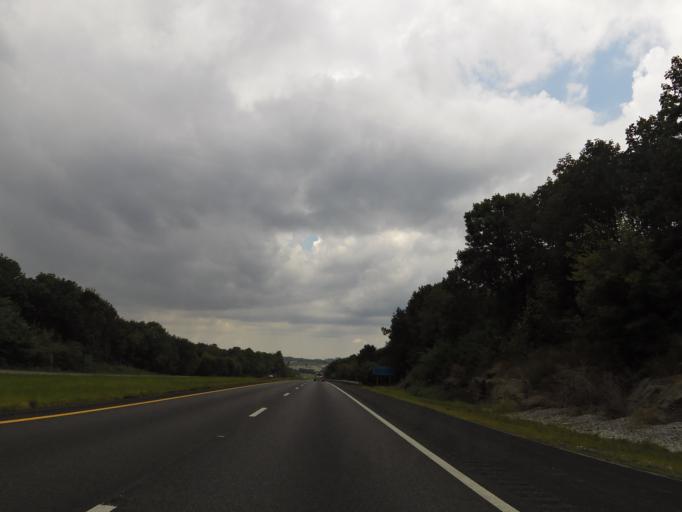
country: US
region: Tennessee
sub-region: Wilson County
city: Watertown
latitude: 36.1833
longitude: -86.1551
